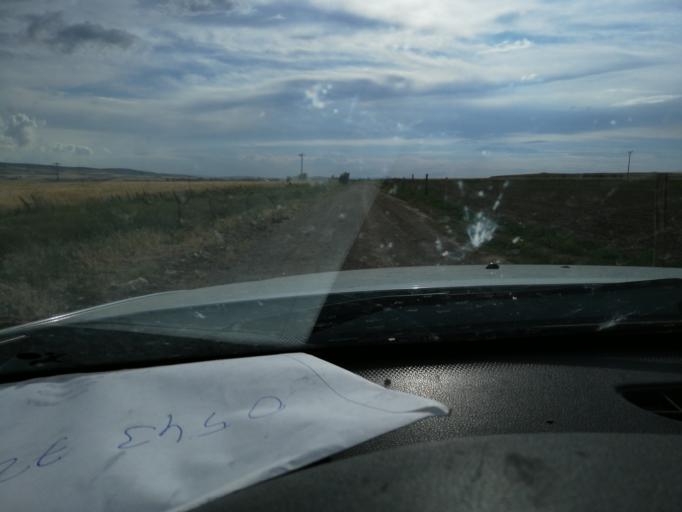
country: TR
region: Kirsehir
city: Kirsehir
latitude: 39.0031
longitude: 34.1220
